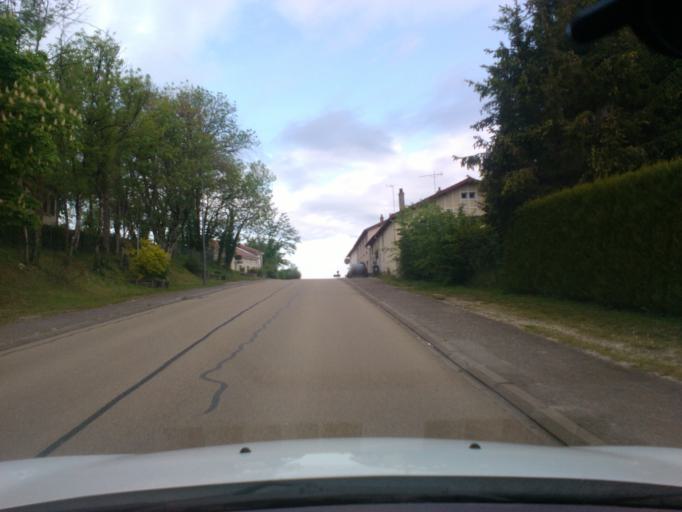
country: FR
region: Champagne-Ardenne
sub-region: Departement de la Haute-Marne
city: Lavilleneuve-au-Roi
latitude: 48.2261
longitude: 4.8865
